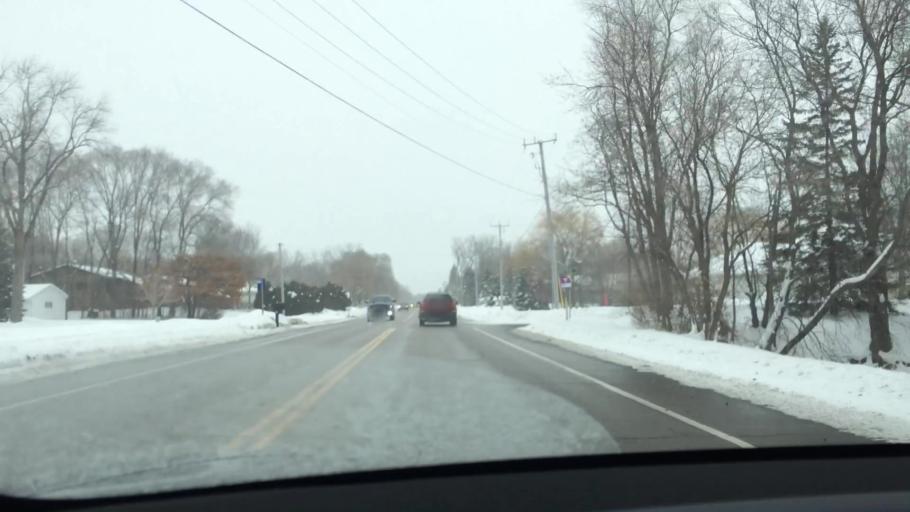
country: US
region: Minnesota
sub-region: Anoka County
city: Circle Pines
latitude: 45.1168
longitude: -93.1274
